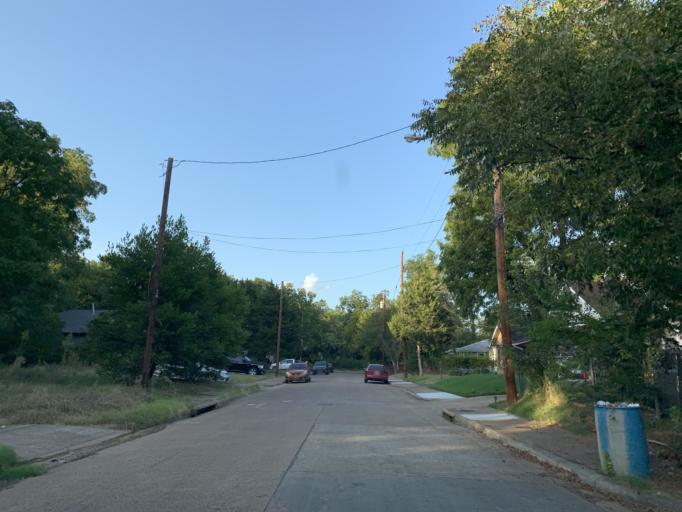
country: US
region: Texas
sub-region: Dallas County
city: Dallas
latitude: 32.7647
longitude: -96.7454
